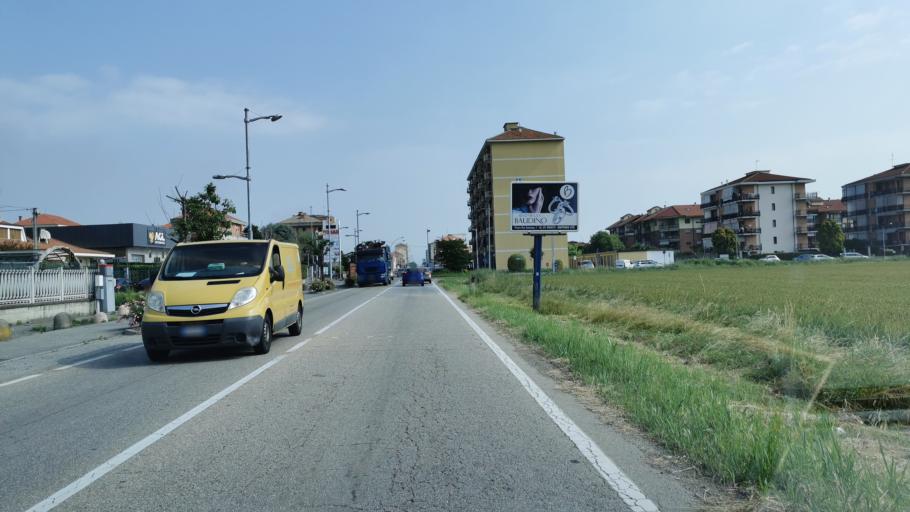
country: IT
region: Piedmont
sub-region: Provincia di Torino
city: Leini
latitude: 45.1421
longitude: 7.7063
